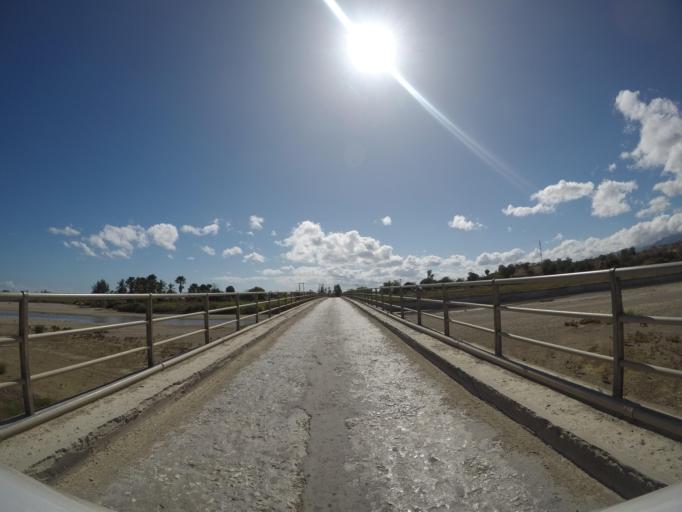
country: TL
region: Baucau
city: Baucau
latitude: -8.4771
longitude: 126.5282
